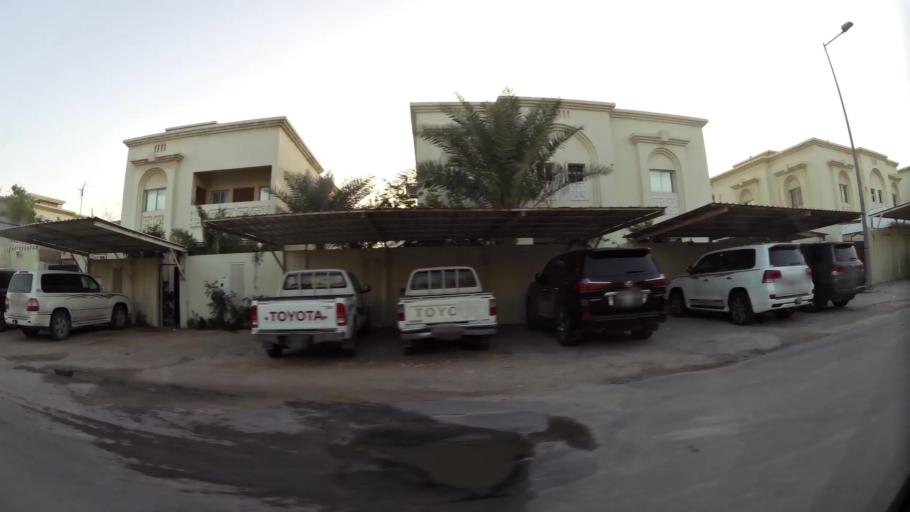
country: QA
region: Baladiyat ar Rayyan
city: Ar Rayyan
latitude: 25.3216
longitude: 51.4651
